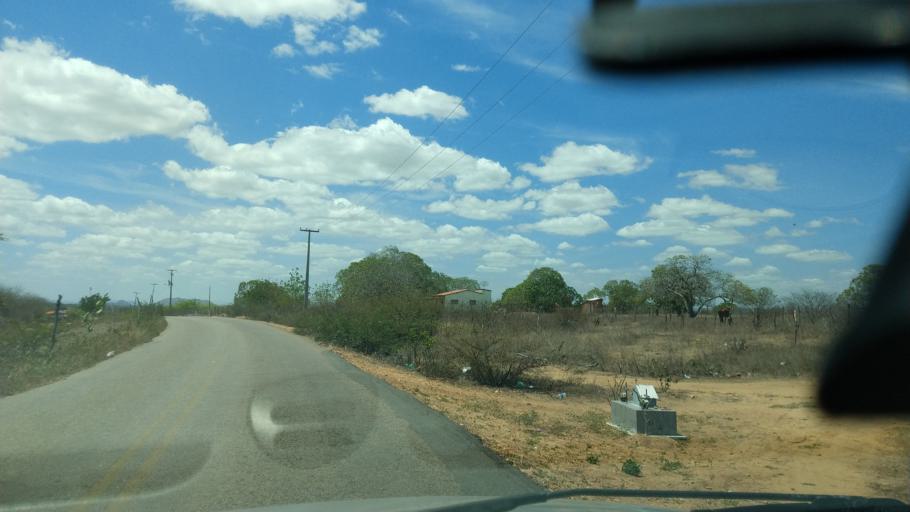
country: BR
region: Rio Grande do Norte
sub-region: Sao Paulo Do Potengi
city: Sao Paulo do Potengi
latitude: -5.9135
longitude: -35.7546
